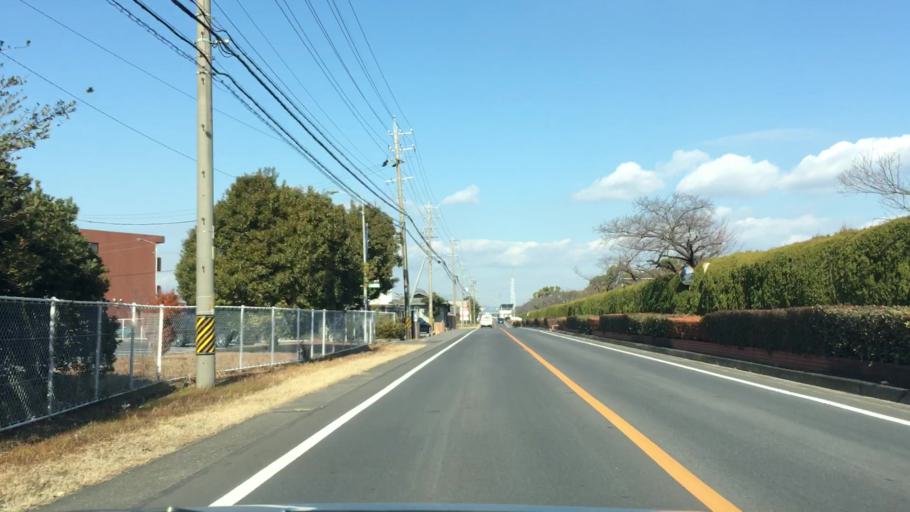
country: JP
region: Aichi
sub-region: Toyota-shi
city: Toyota
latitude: 35.0244
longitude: 137.1277
